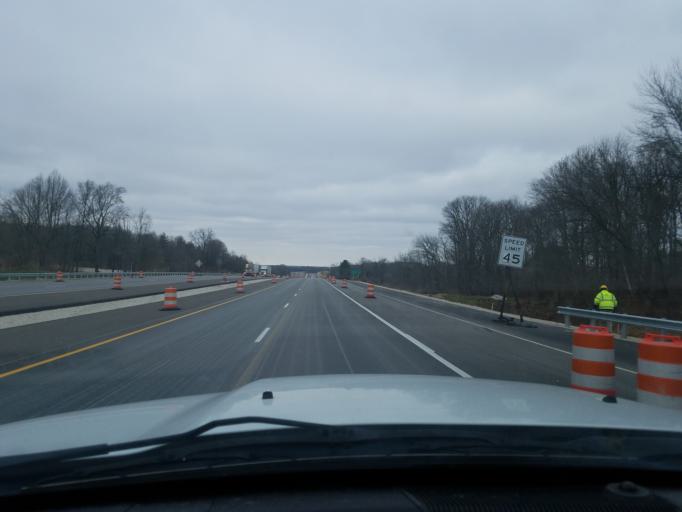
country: US
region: Indiana
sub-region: Monroe County
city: Bloomington
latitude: 39.1962
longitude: -86.5542
